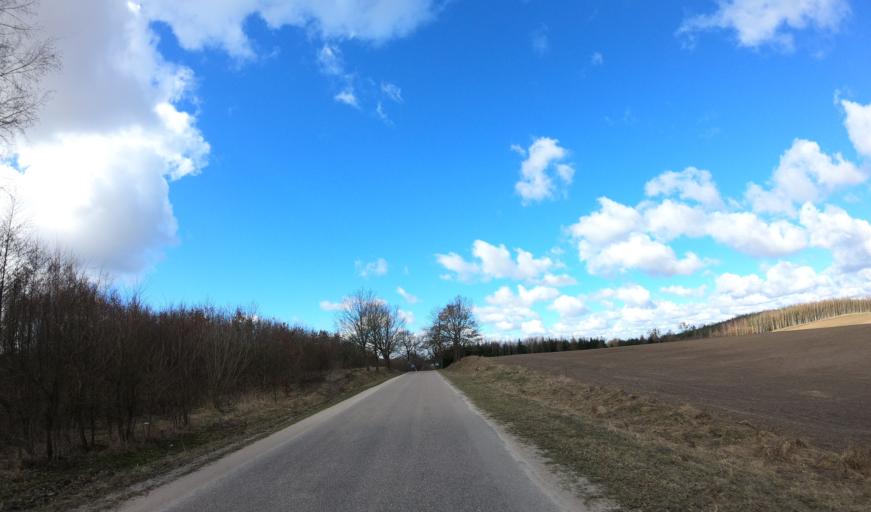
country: PL
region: West Pomeranian Voivodeship
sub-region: Powiat drawski
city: Zlocieniec
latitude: 53.4822
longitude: 15.9175
